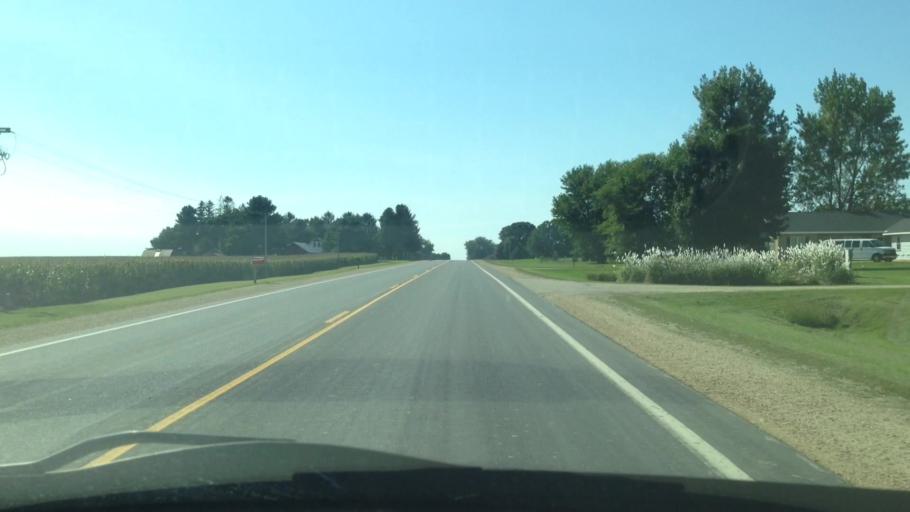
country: US
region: Minnesota
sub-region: Winona County
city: Lewiston
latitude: 43.9696
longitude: -91.8243
